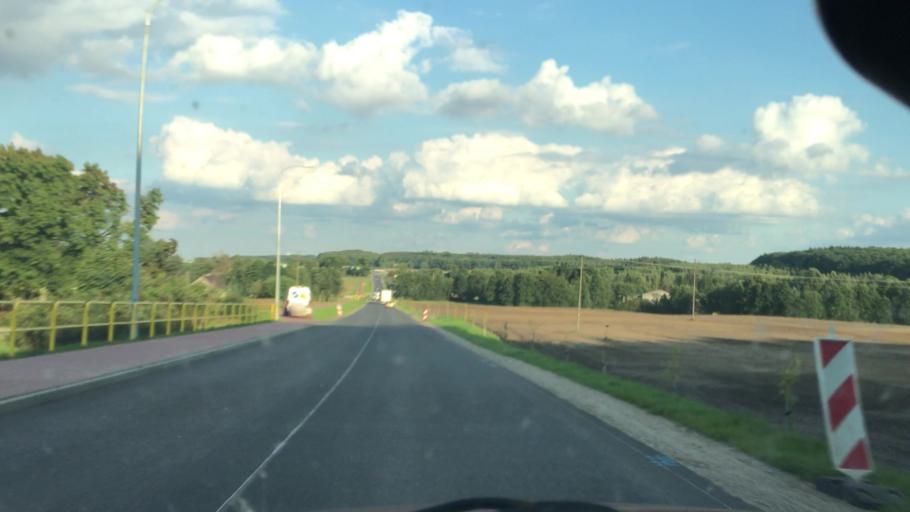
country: PL
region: Pomeranian Voivodeship
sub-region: Powiat tczewski
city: Pelplin
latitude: 53.9286
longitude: 18.6240
